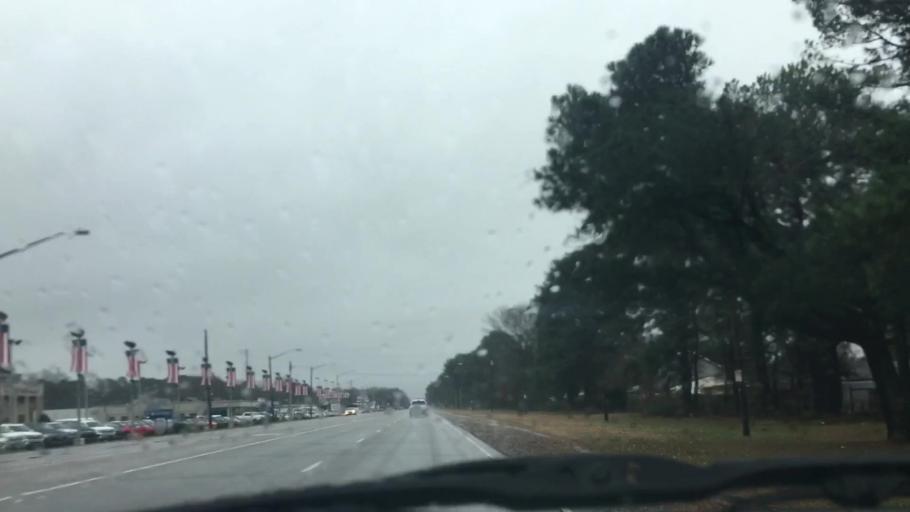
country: US
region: Virginia
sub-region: City of Norfolk
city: Norfolk
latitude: 36.9131
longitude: -76.2371
